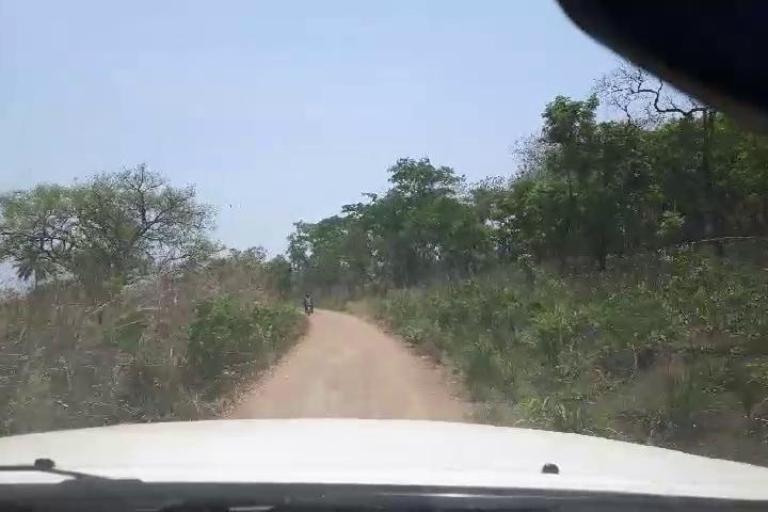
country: SL
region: Northern Province
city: Alikalia
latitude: 9.0832
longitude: -11.4673
